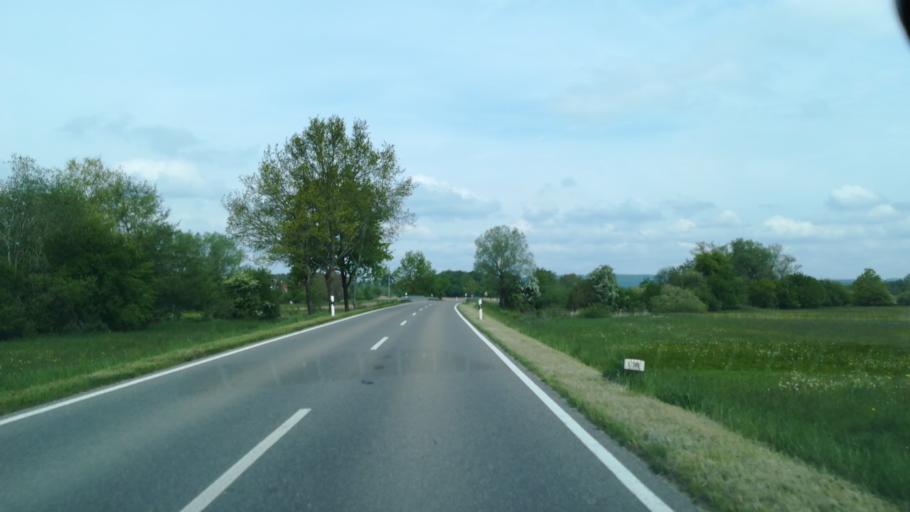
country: DE
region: Baden-Wuerttemberg
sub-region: Freiburg Region
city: Volkertshausen
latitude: 47.8027
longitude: 8.8790
